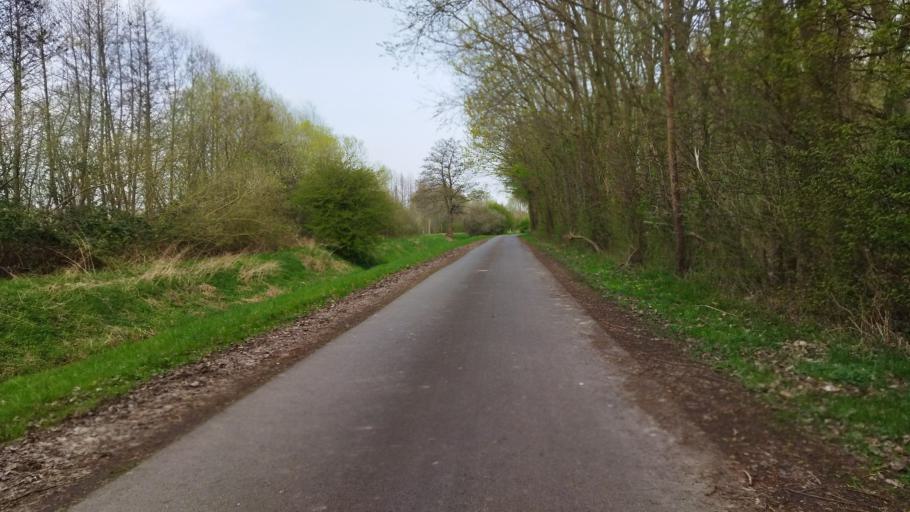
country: DE
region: Lower Saxony
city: Raddestorf
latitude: 52.4323
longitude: 8.9739
